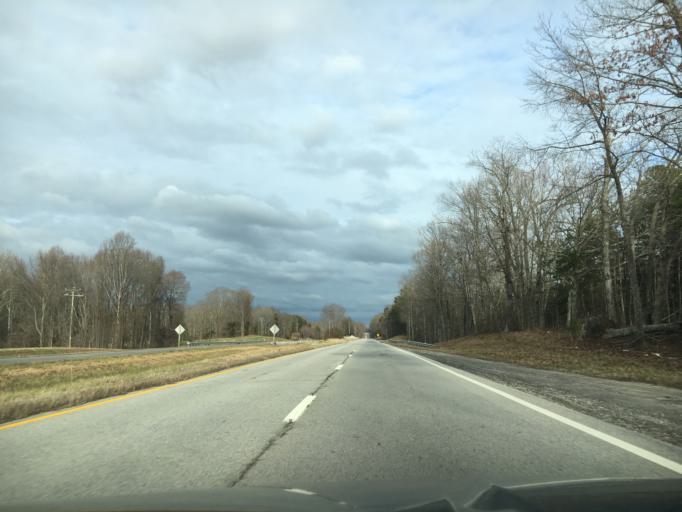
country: US
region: Virginia
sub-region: Nottoway County
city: Crewe
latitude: 37.1527
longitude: -78.2810
